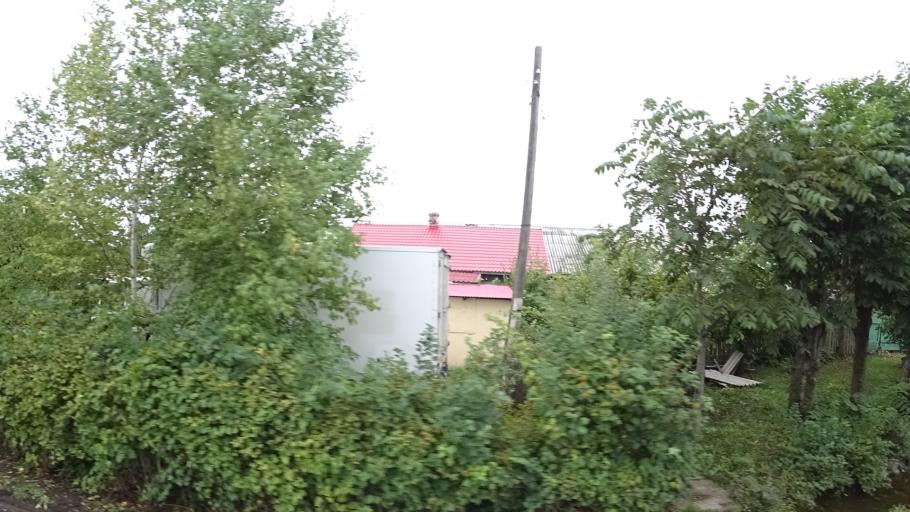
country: RU
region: Primorskiy
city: Chernigovka
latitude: 44.3466
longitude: 132.5791
